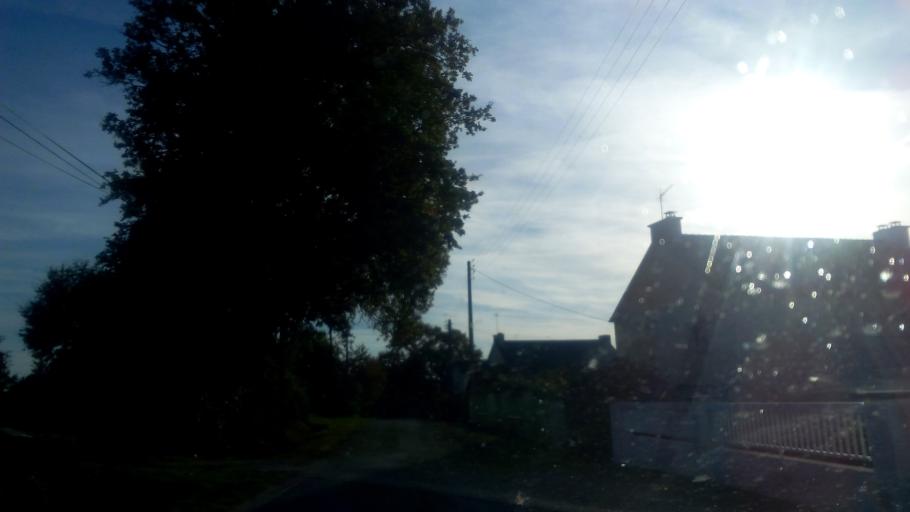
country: FR
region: Brittany
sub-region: Departement du Morbihan
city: Saint-Perreux
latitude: 47.6999
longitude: -2.1152
